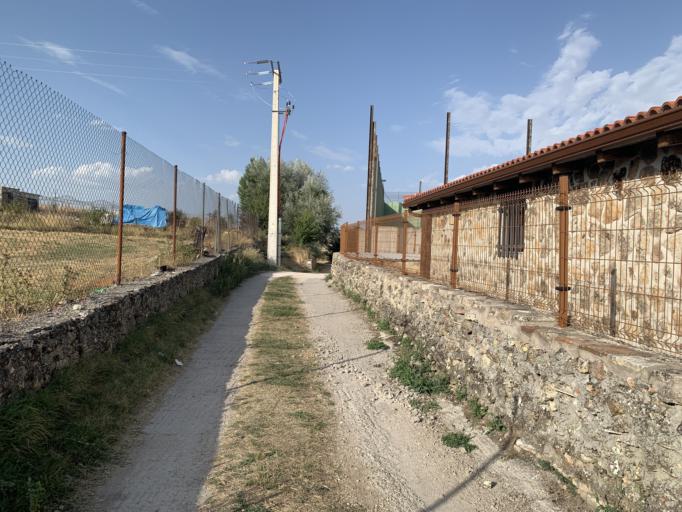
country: ES
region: Castille-La Mancha
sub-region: Provincia de Guadalajara
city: Sacecorbo
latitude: 40.8340
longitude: -2.4177
